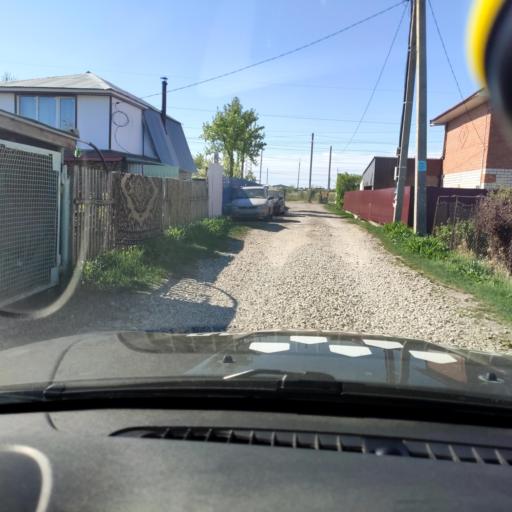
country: RU
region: Samara
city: Tol'yatti
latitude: 53.5926
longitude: 49.2890
